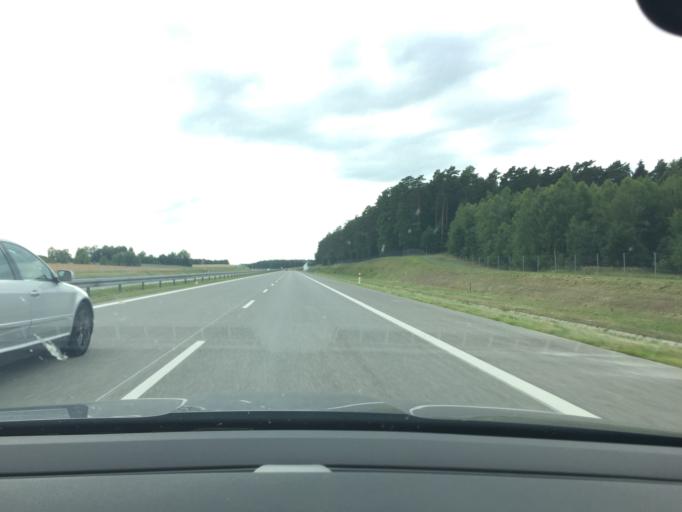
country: PL
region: Lubusz
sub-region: Powiat swiebodzinski
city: Lubrza
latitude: 52.3182
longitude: 15.4229
